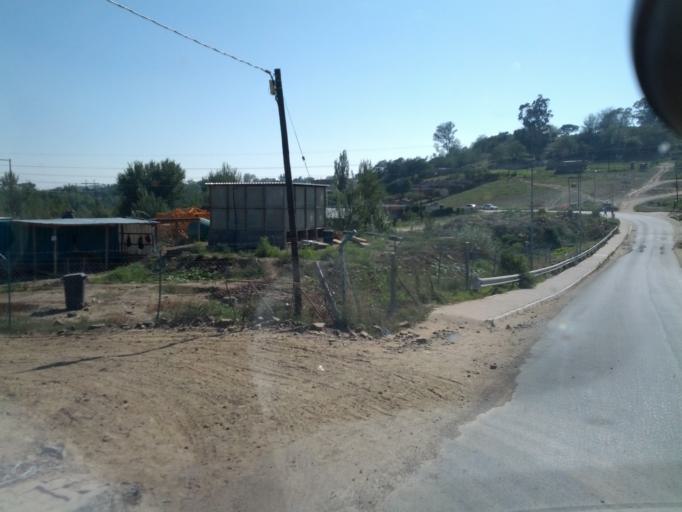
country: LS
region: Maseru
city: Maseru
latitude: -29.3041
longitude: 27.4885
